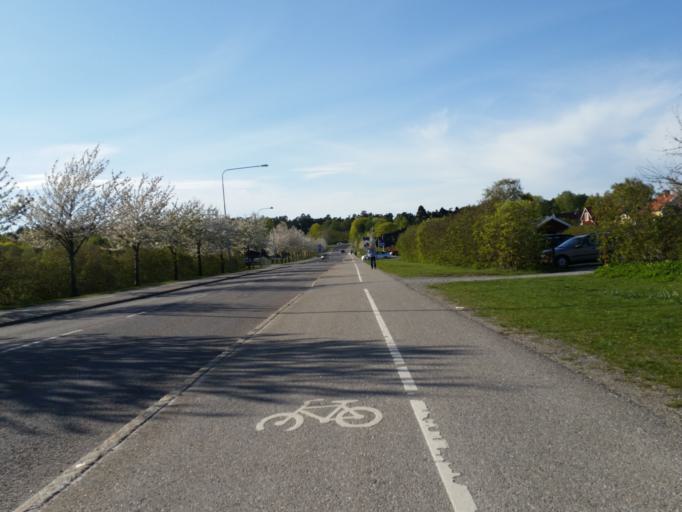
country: SE
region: Stockholm
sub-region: Nacka Kommun
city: Nacka
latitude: 59.2690
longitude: 18.1153
